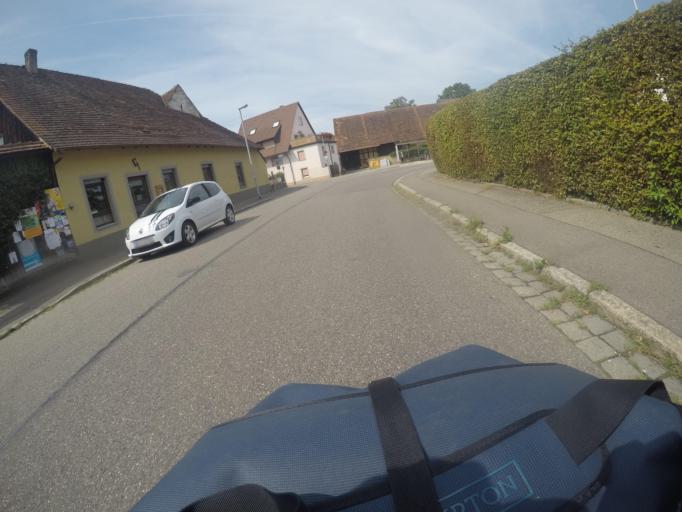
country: DE
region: Baden-Wuerttemberg
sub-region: Freiburg Region
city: Ebringen
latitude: 47.9773
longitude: 7.7954
